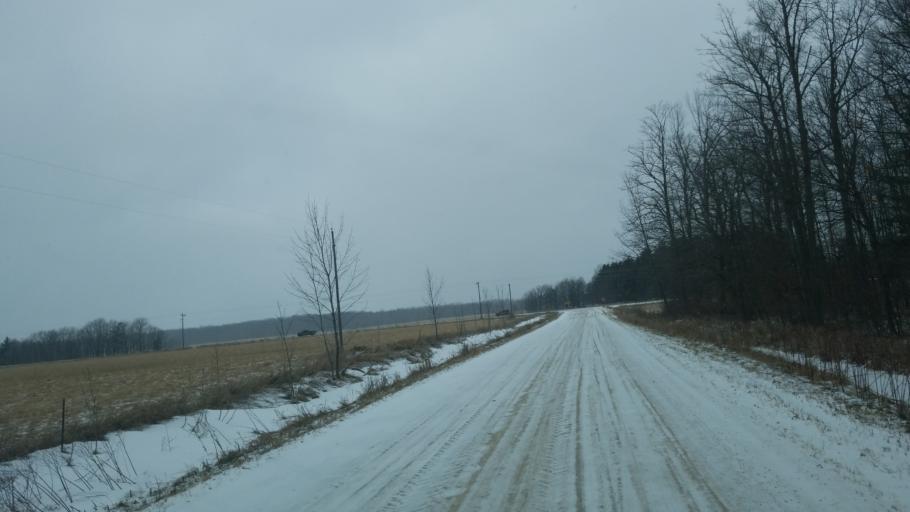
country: US
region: Michigan
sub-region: Osceola County
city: Evart
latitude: 44.0285
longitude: -85.2066
